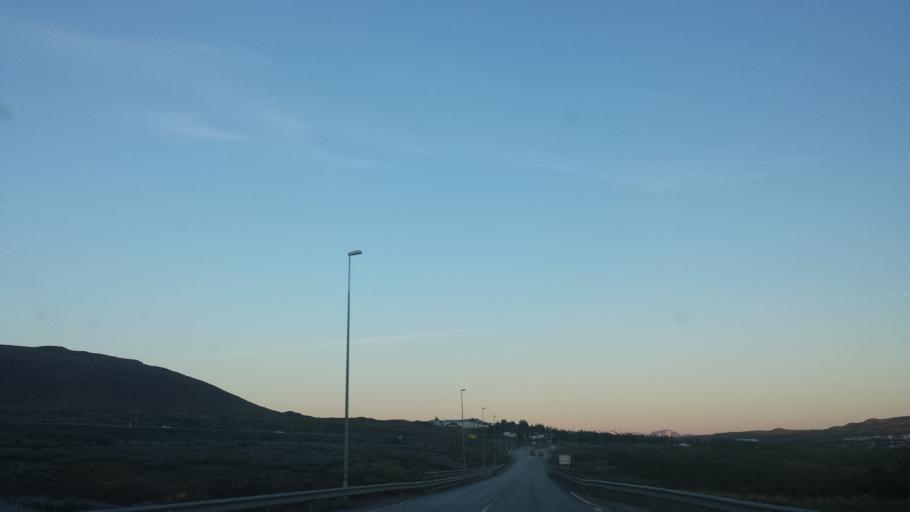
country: IS
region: Capital Region
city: Mosfellsbaer
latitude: 64.1812
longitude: -21.6790
